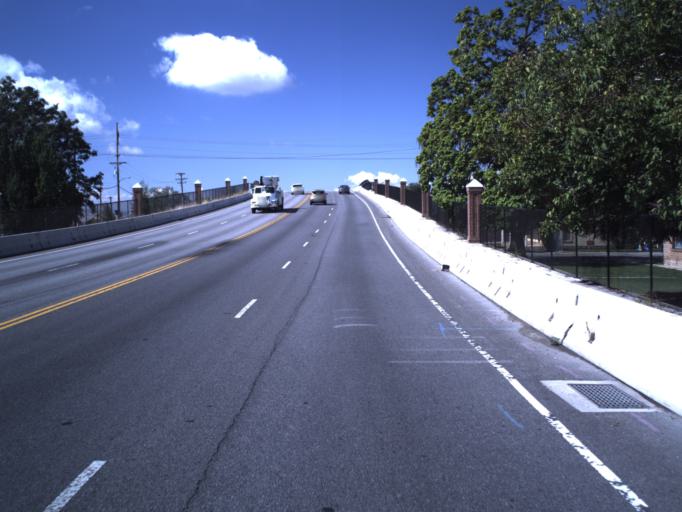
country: US
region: Utah
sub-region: Utah County
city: Springville
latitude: 40.1612
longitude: -111.6154
